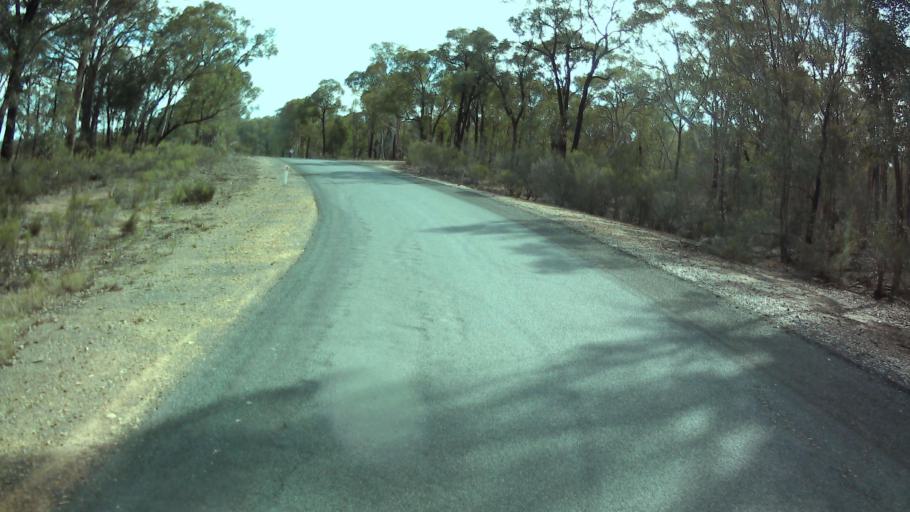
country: AU
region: New South Wales
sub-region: Weddin
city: Grenfell
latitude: -33.8643
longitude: 148.2118
